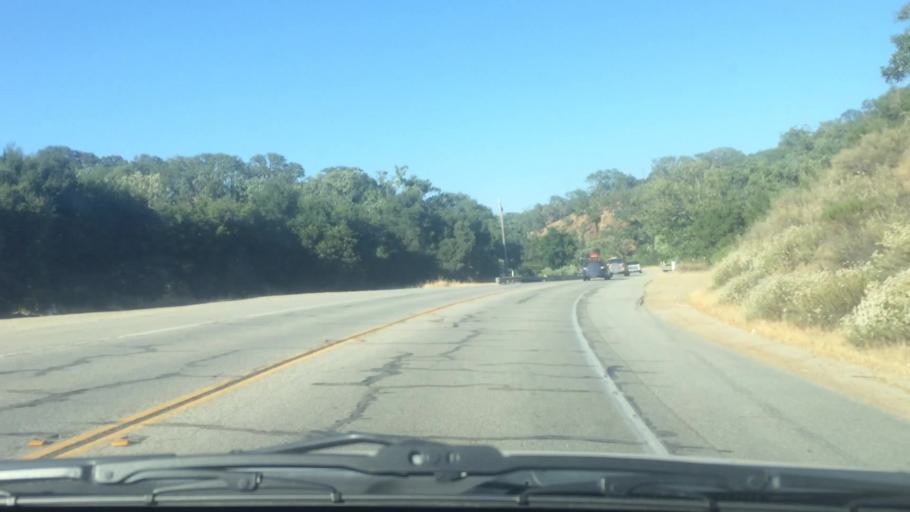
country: US
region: California
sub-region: San Luis Obispo County
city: Atascadero
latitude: 35.4559
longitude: -120.6906
